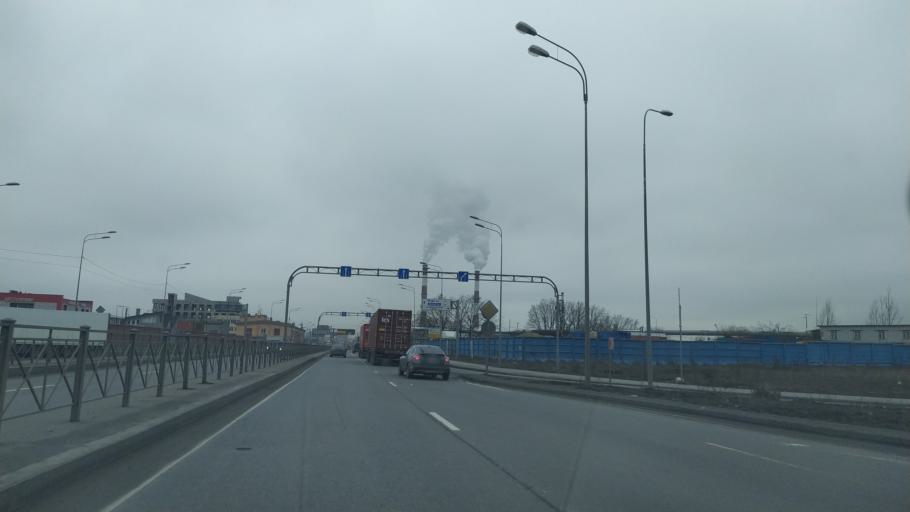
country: RU
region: St.-Petersburg
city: Kupchino
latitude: 59.8324
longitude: 30.3089
